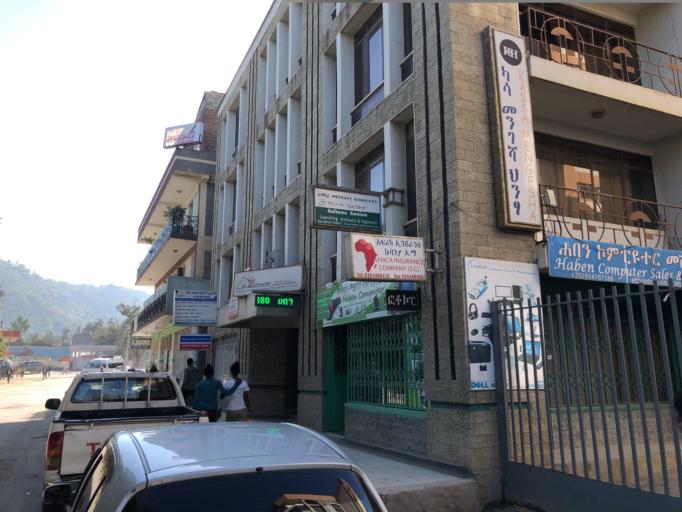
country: ET
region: Tigray
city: Mekele
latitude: 13.4963
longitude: 39.4772
